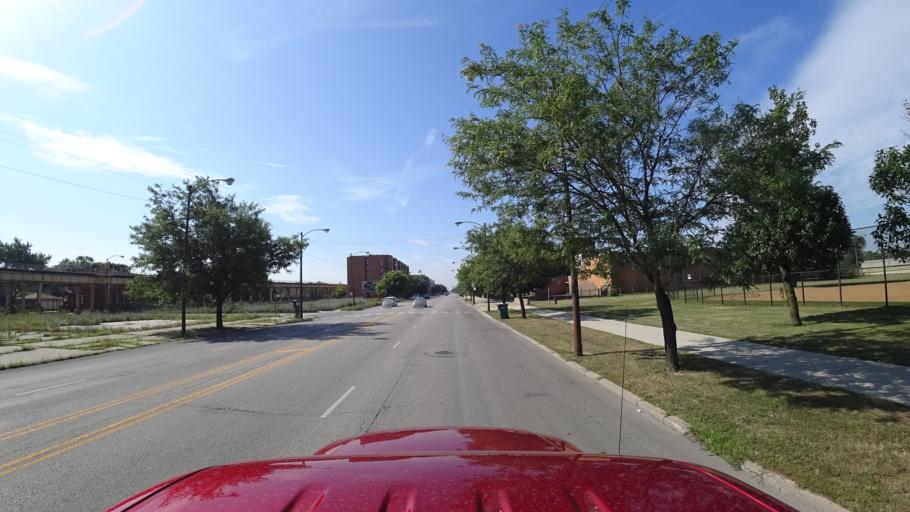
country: US
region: Illinois
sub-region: Cook County
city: Chicago
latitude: 41.8261
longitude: -87.6265
